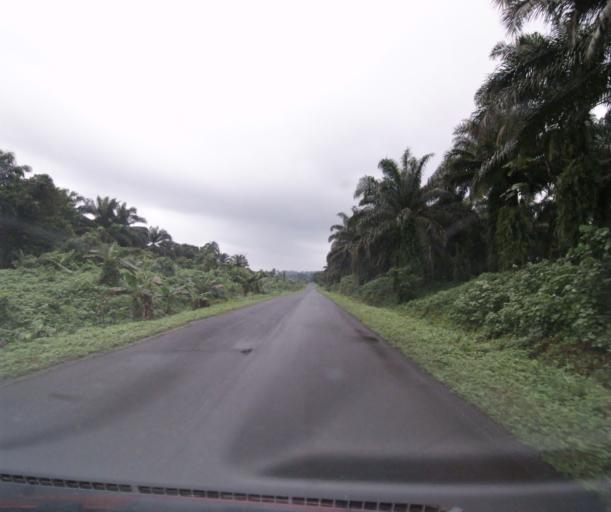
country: CM
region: South-West Province
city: Idenao
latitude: 4.1371
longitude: 8.9899
